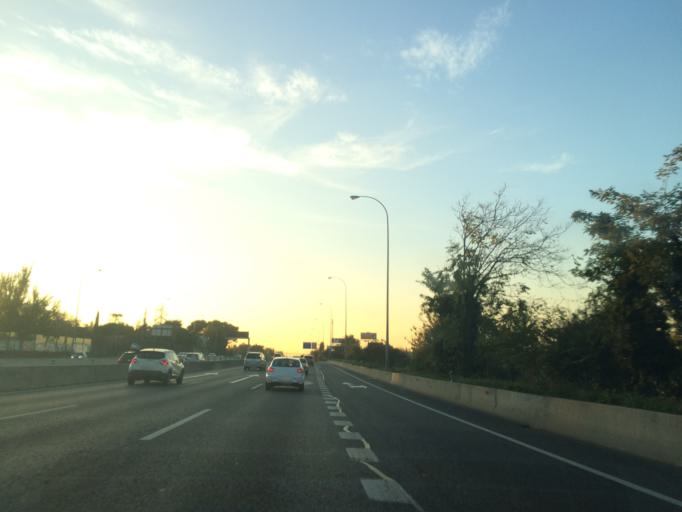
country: ES
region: Madrid
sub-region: Provincia de Madrid
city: Moncloa-Aravaca
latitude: 40.4625
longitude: -3.7725
